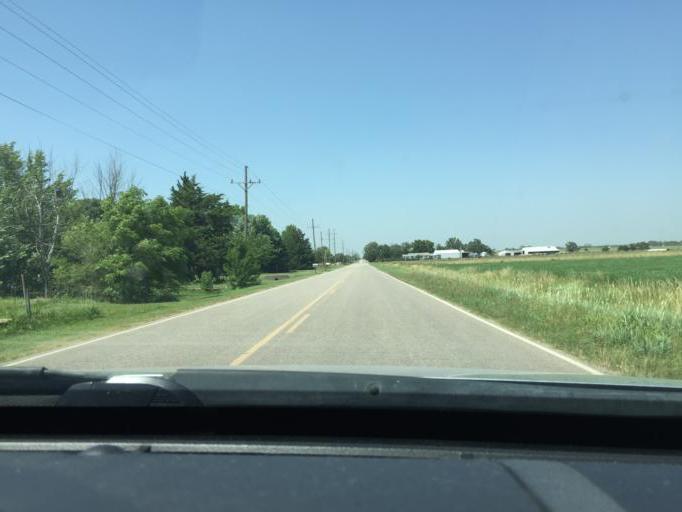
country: US
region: Kansas
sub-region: Reno County
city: Haven
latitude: 37.9272
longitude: -97.8853
